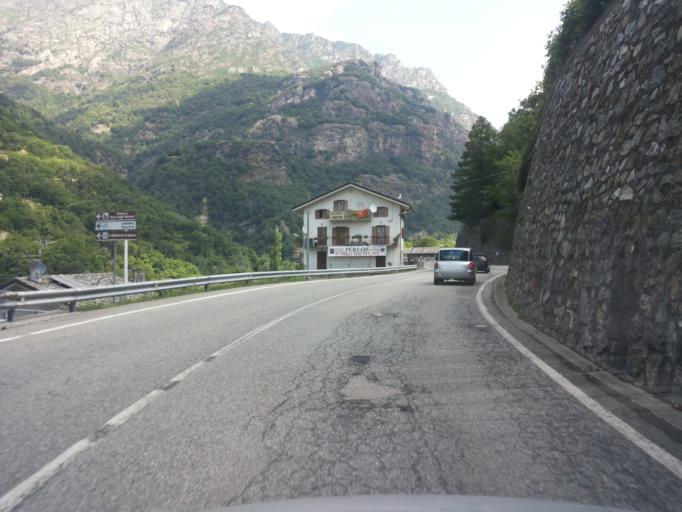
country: IT
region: Aosta Valley
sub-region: Valle d'Aosta
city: Perloz
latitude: 45.6152
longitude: 7.8153
